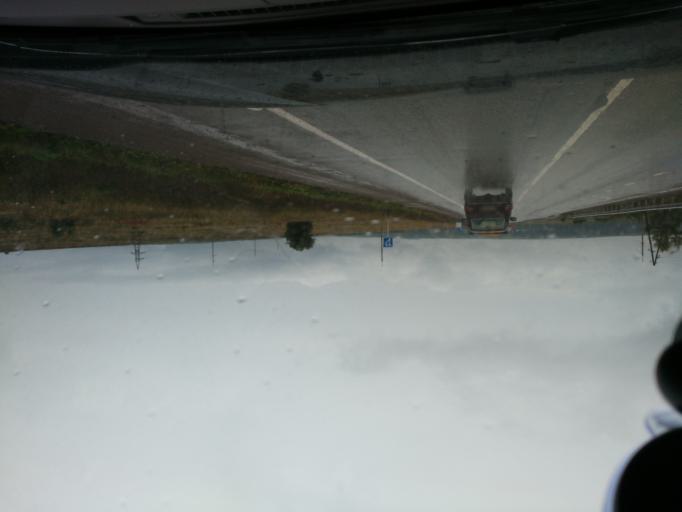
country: RU
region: Perm
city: Yugo-Kamskiy
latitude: 57.7000
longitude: 55.6222
